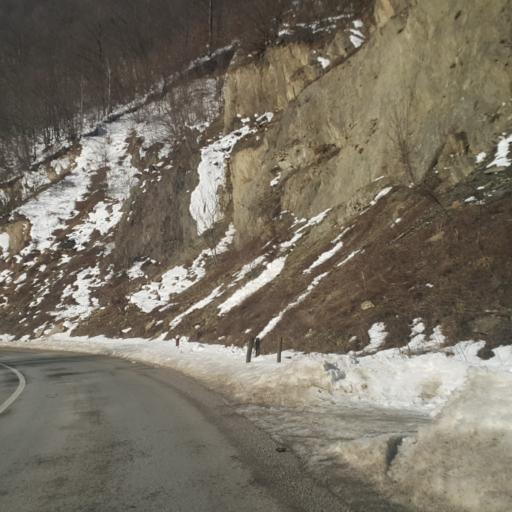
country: RS
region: Central Serbia
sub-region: Rasinski Okrug
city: Aleksandrovac
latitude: 43.3142
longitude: 20.9174
